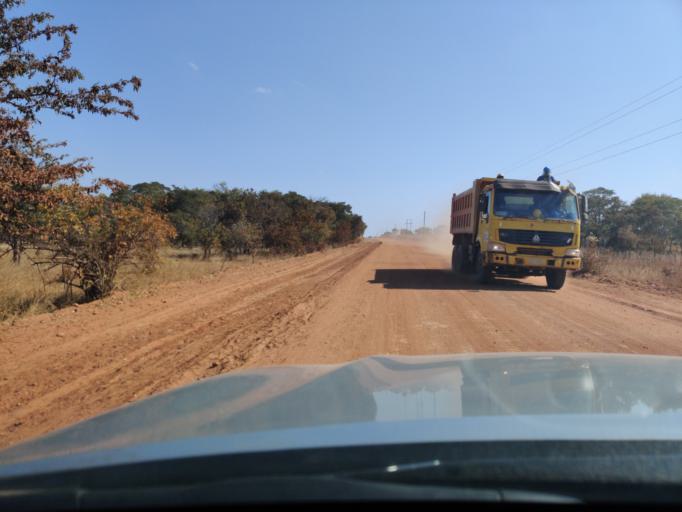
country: ZM
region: Central
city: Mkushi
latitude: -13.9908
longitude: 29.5315
